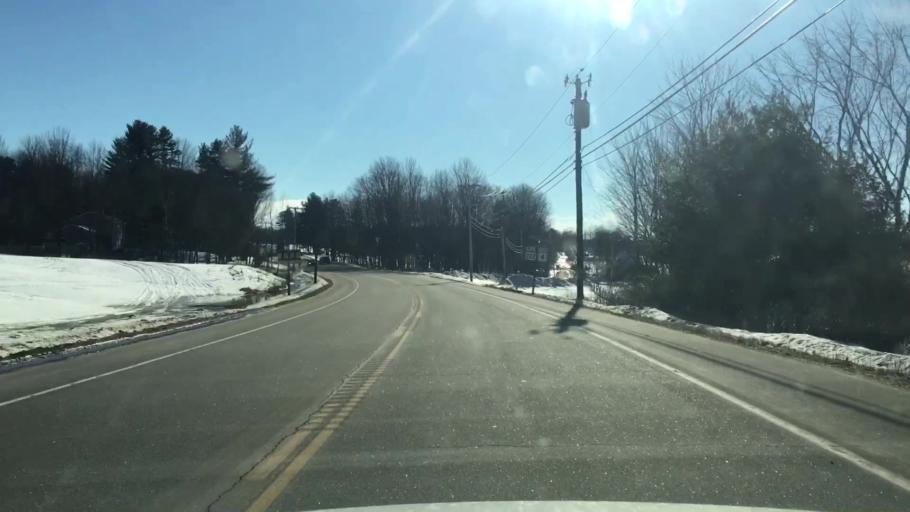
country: US
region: Maine
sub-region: Cumberland County
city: North Windham
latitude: 43.8102
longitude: -70.4027
